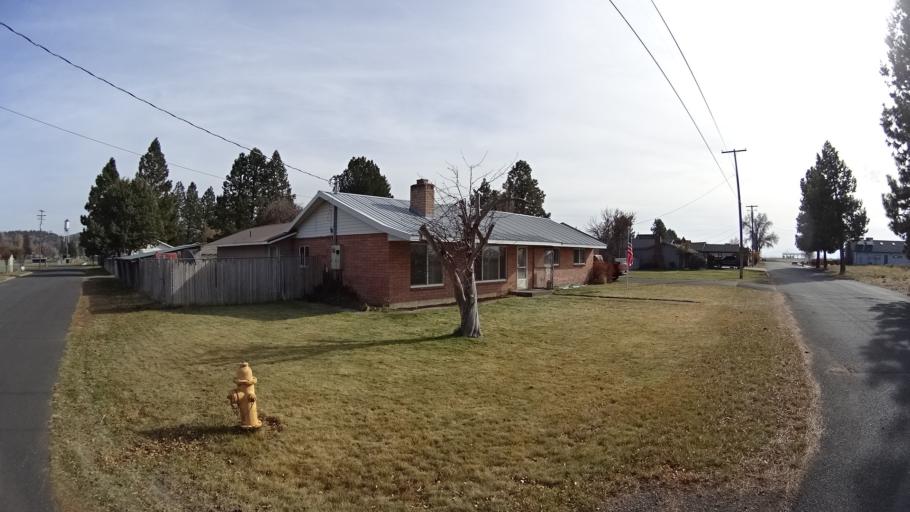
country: US
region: Oregon
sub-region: Klamath County
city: Klamath Falls
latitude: 41.9656
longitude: -121.9266
